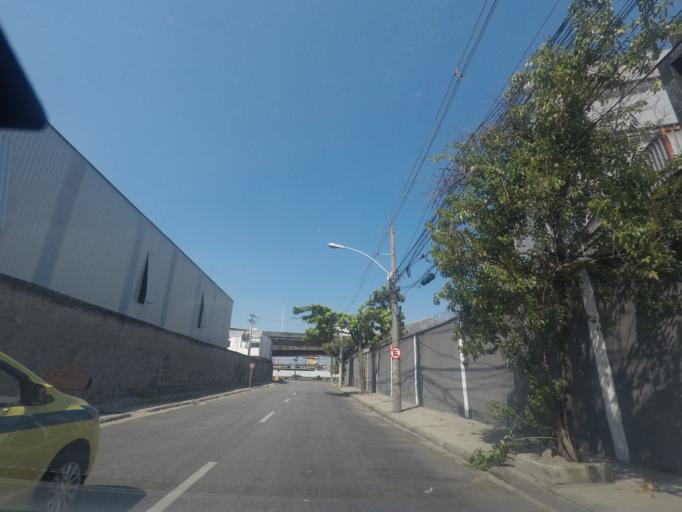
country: BR
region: Rio de Janeiro
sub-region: Rio De Janeiro
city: Rio de Janeiro
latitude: -22.8903
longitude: -43.2188
